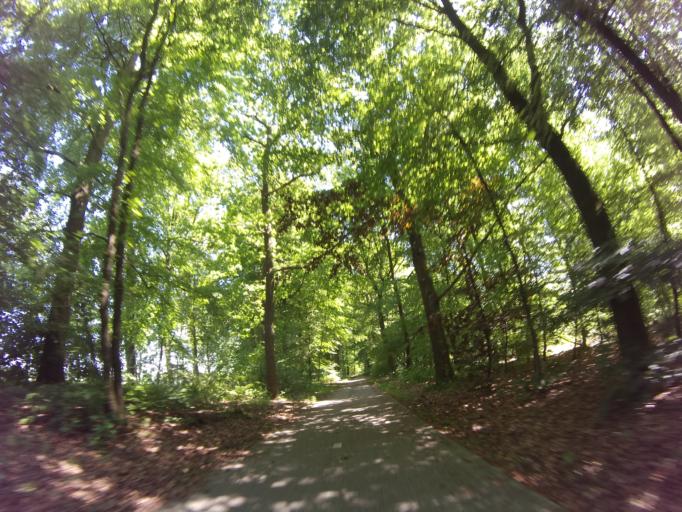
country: NL
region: Drenthe
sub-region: Gemeente Coevorden
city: Dalen
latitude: 52.7801
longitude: 6.6472
